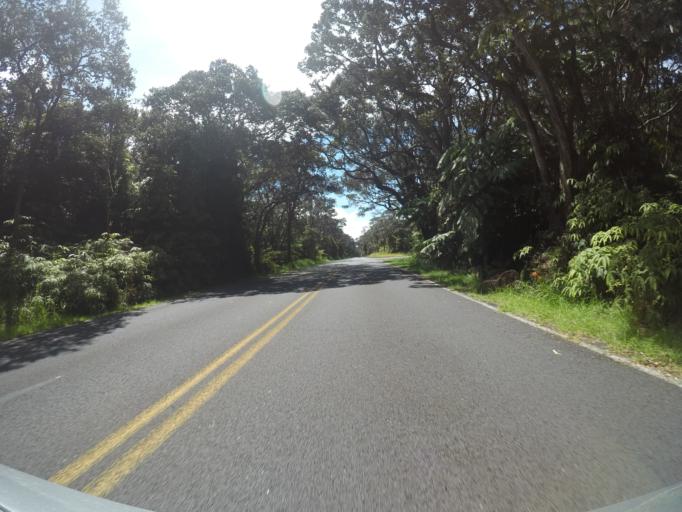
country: US
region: Hawaii
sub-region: Hawaii County
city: Volcano
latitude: 19.4273
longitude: -155.2541
